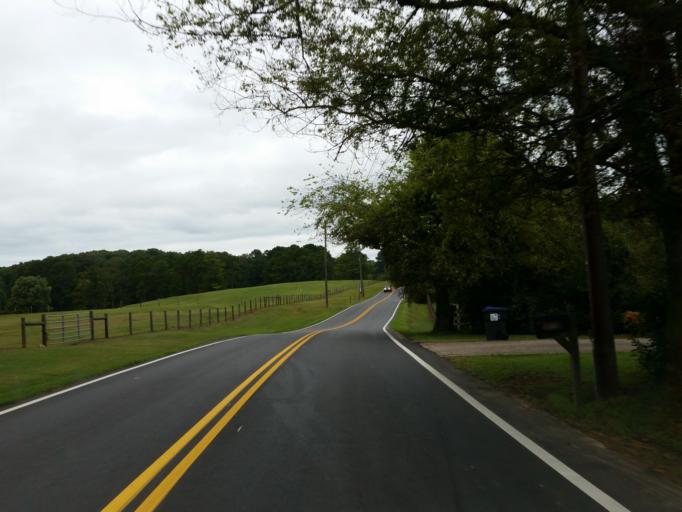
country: US
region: Georgia
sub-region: Cherokee County
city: Woodstock
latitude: 34.0415
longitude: -84.5107
